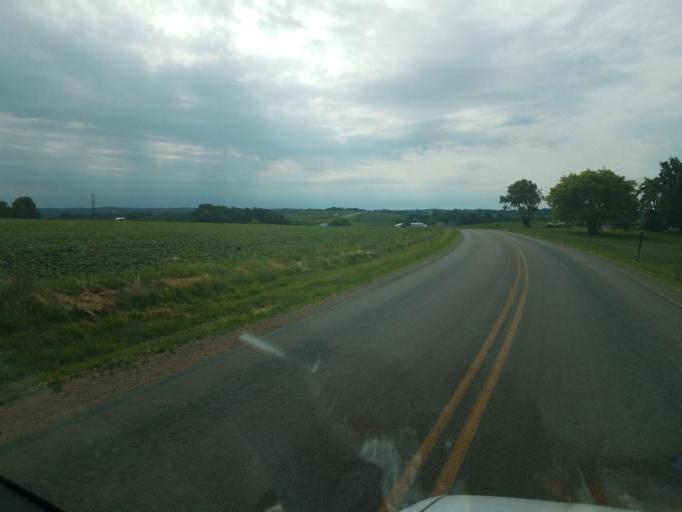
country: US
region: Wisconsin
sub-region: Vernon County
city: Hillsboro
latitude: 43.6074
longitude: -90.4360
